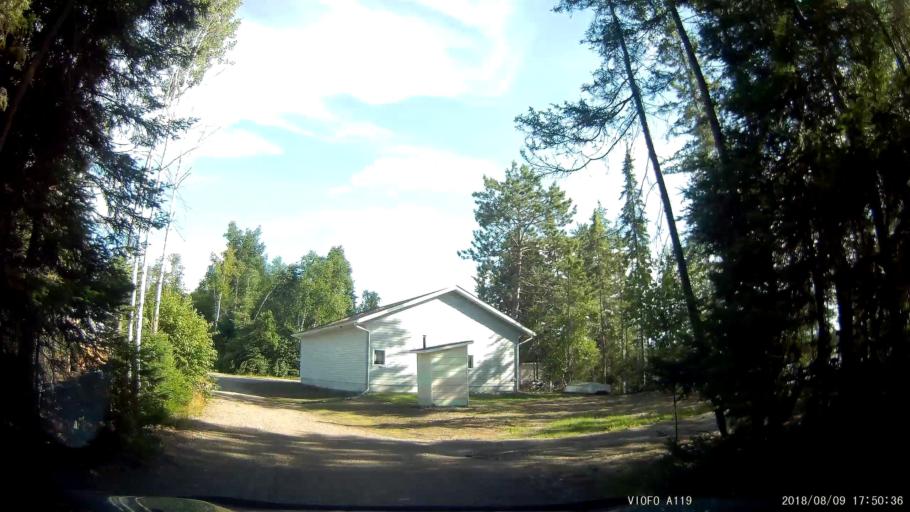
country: CA
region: Ontario
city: Rayside-Balfour
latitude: 46.5852
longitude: -81.5455
